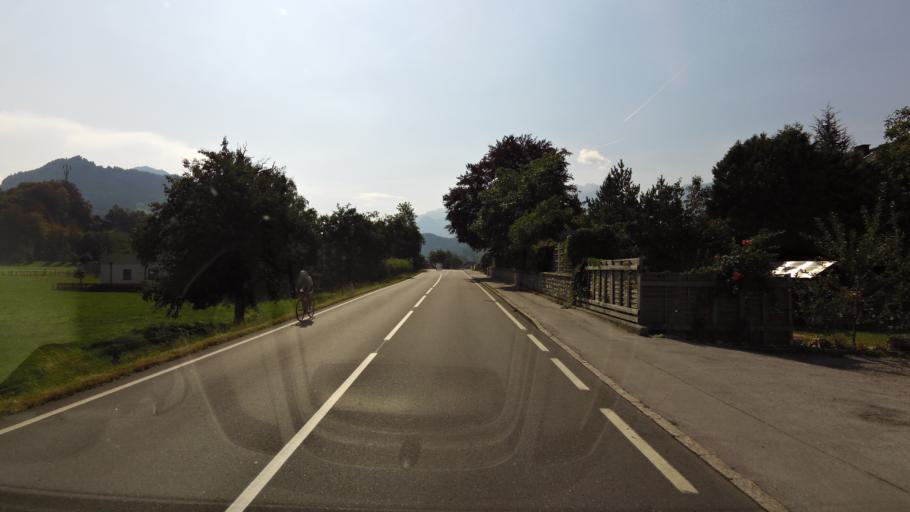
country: AT
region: Salzburg
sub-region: Politischer Bezirk Hallein
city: Golling an der Salzach
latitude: 47.6155
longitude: 13.1633
